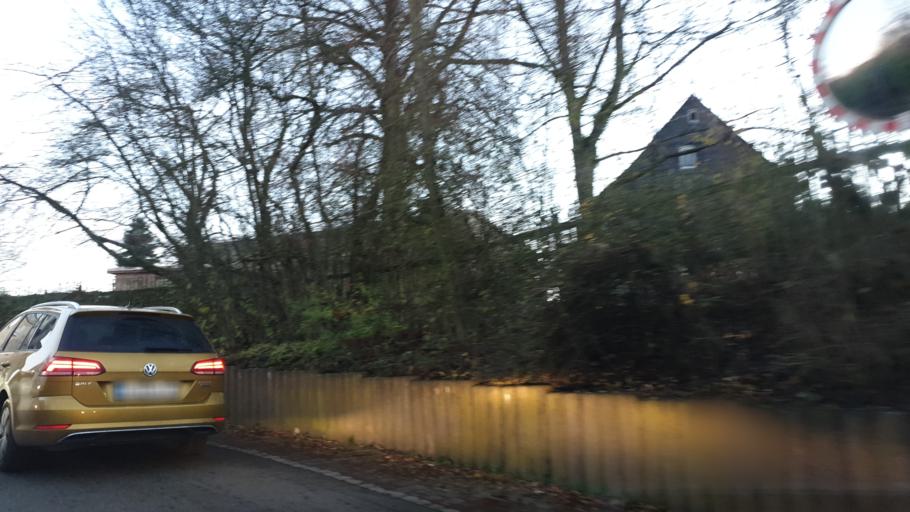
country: DE
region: Saxony
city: Hohndorf
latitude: 50.7431
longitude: 12.6746
